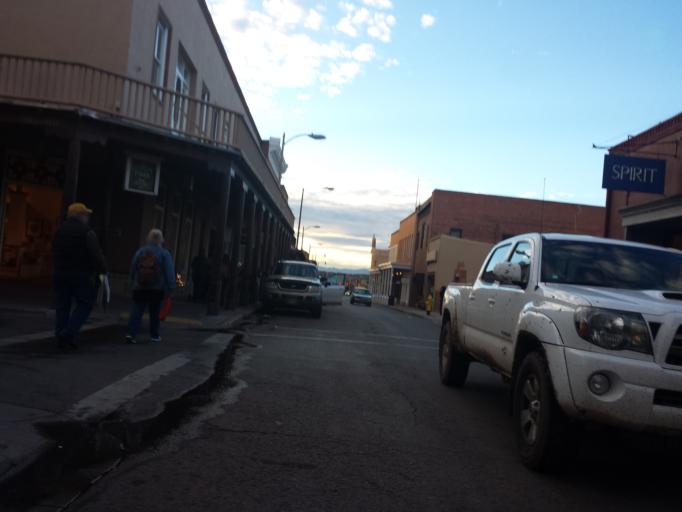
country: US
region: New Mexico
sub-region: Santa Fe County
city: Santa Fe
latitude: 35.6873
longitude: -105.9395
